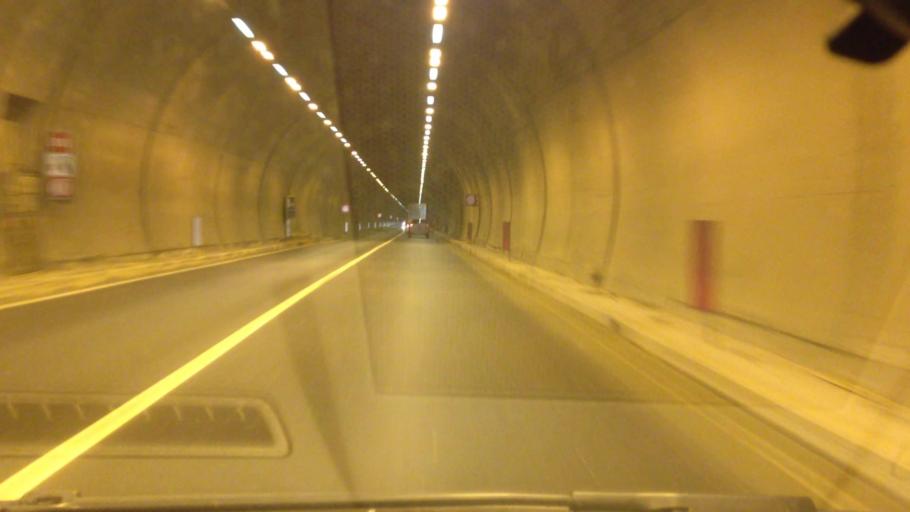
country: IT
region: Piedmont
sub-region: Provincia di Asti
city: Piano-Molini d'Isola
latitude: 44.8327
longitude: 8.2010
